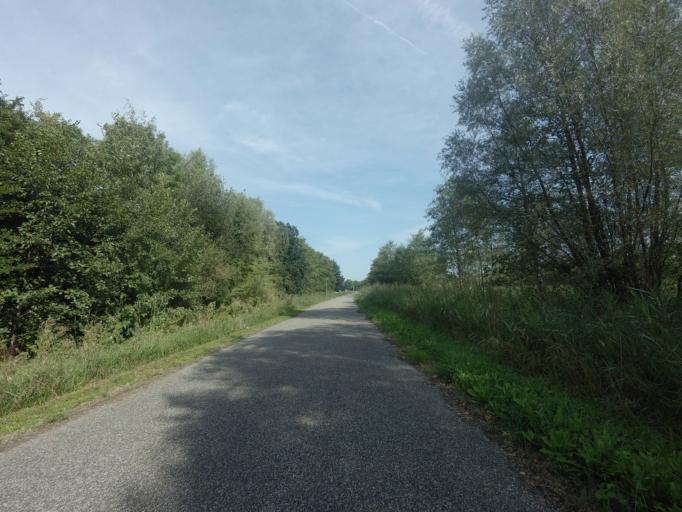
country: NL
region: Groningen
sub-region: Gemeente Leek
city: Leek
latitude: 53.1804
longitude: 6.3801
